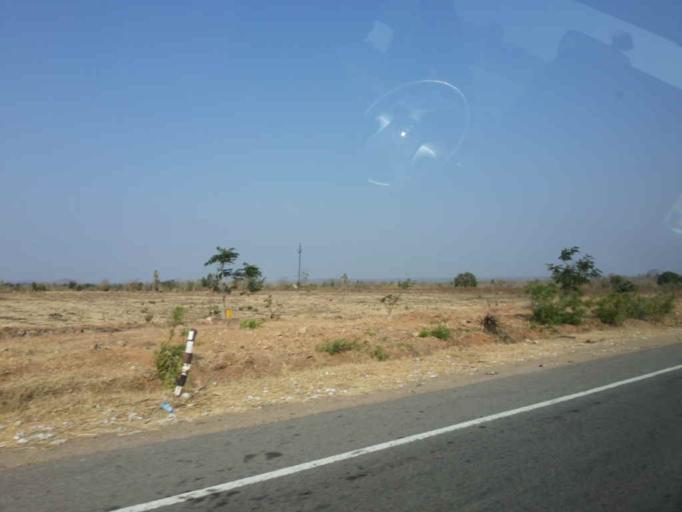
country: IN
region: Telangana
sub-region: Nizamabad District
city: Kamareddi
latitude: 18.4719
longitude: 78.2222
